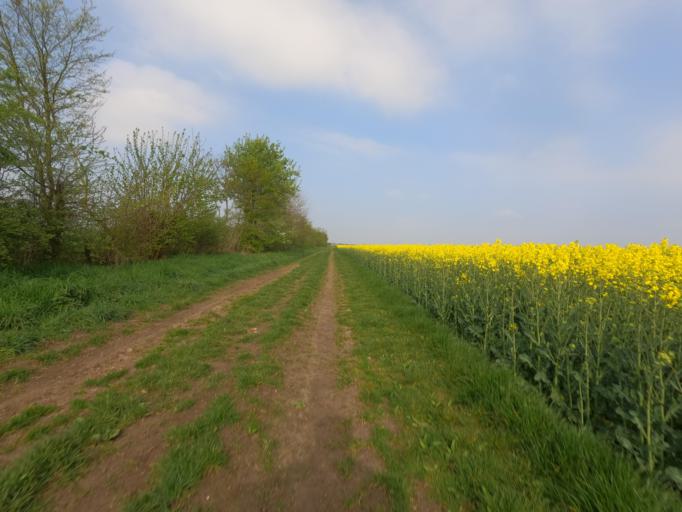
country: DE
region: North Rhine-Westphalia
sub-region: Regierungsbezirk Koln
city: Heinsberg
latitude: 51.0434
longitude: 6.1157
